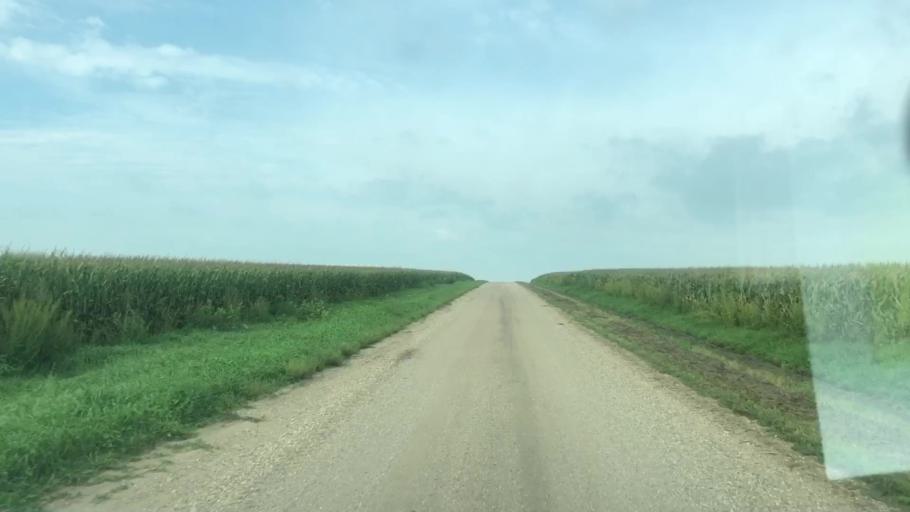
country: US
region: Iowa
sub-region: Lyon County
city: George
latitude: 43.2725
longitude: -95.9906
